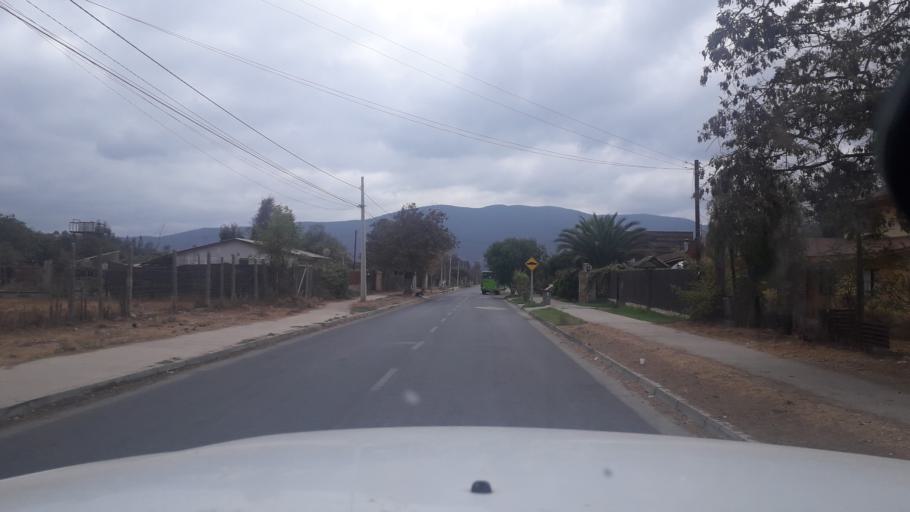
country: CL
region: Valparaiso
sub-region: Provincia de Marga Marga
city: Limache
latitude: -33.0185
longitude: -71.2694
